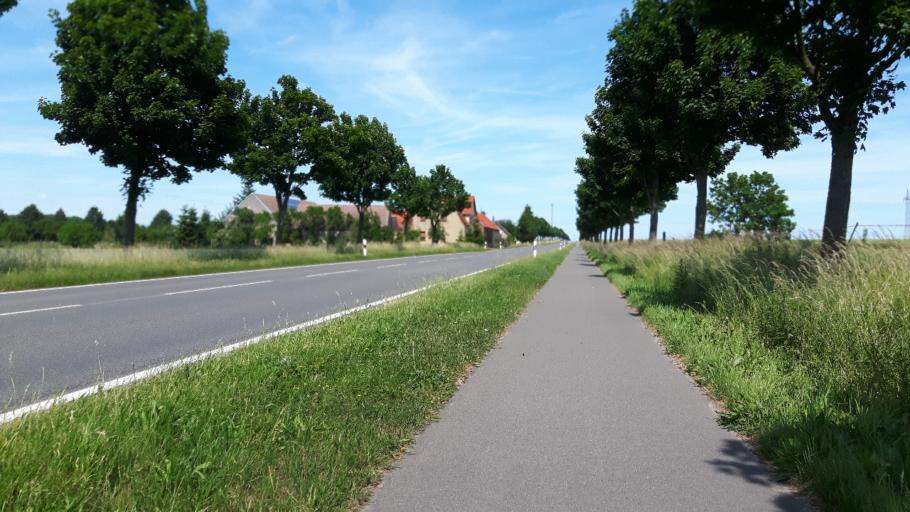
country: DE
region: Saxony-Anhalt
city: Kropstadt
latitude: 52.0148
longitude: 12.7898
